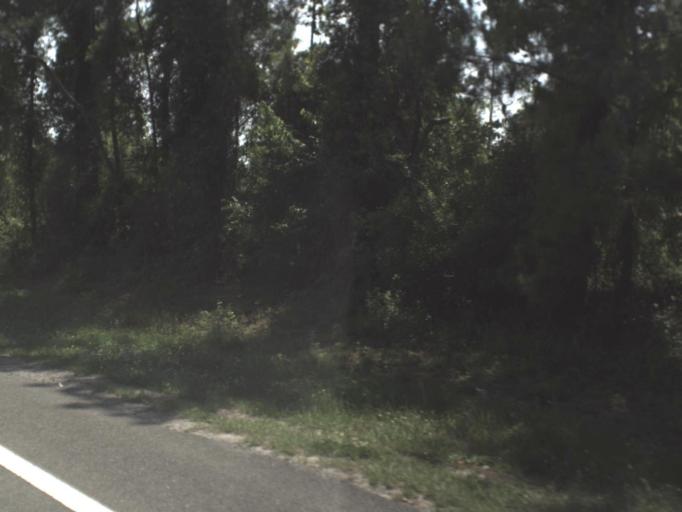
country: US
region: Florida
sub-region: Nassau County
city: Yulee
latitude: 30.5475
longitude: -81.6214
